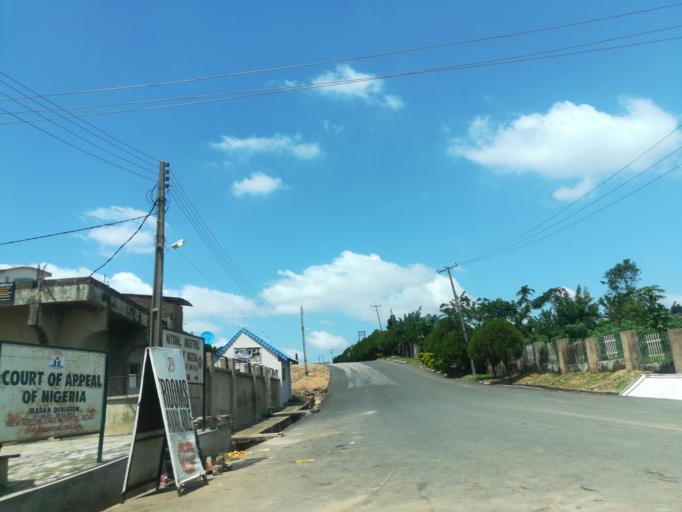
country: NG
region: Oyo
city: Ibadan
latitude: 7.3549
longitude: 3.8652
